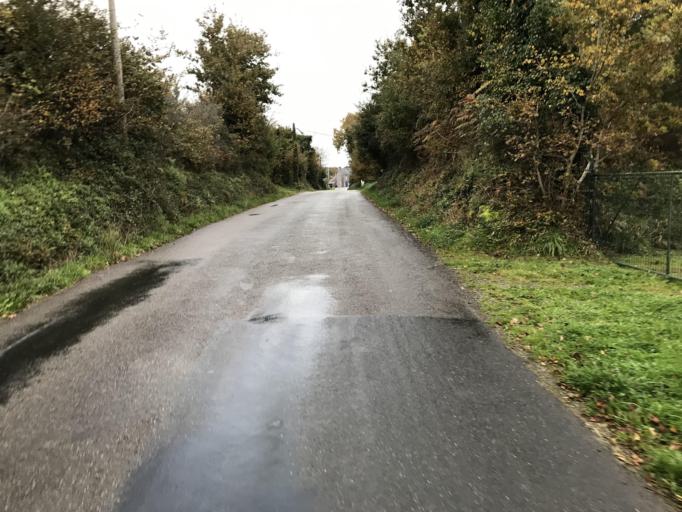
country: FR
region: Brittany
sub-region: Departement du Finistere
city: Logonna-Daoulas
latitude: 48.3346
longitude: -4.3022
